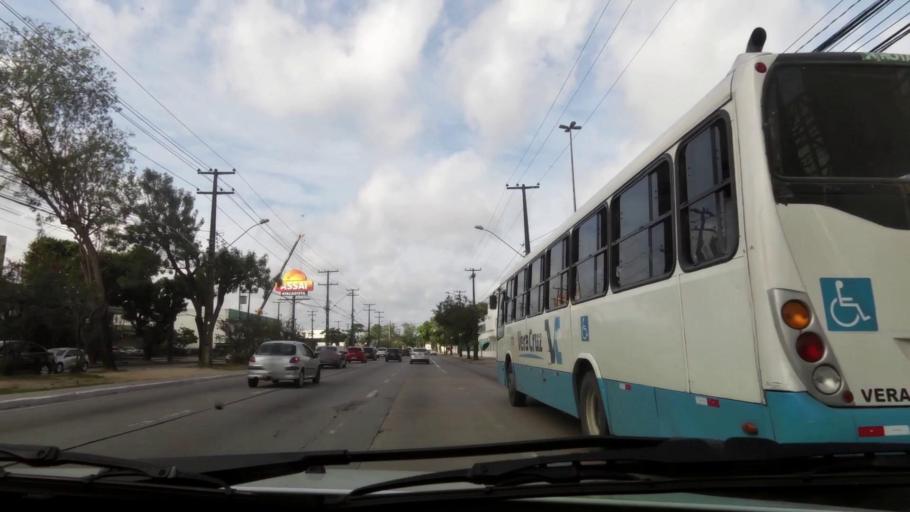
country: BR
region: Pernambuco
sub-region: Recife
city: Recife
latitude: -8.0996
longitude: -34.9101
